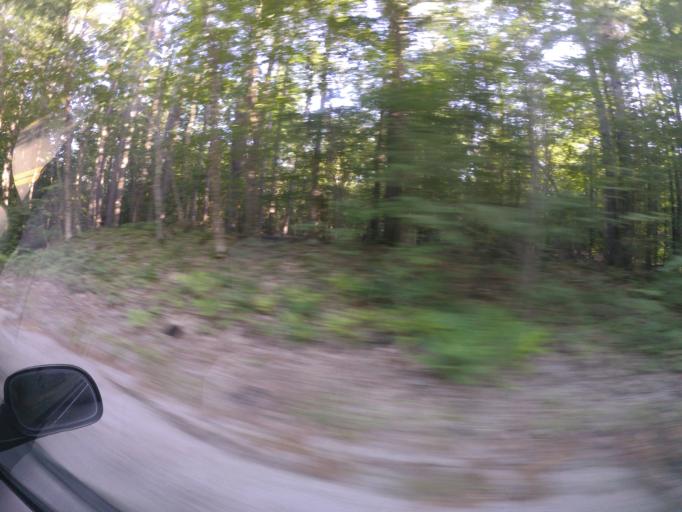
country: US
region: Maine
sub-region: Cumberland County
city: Raymond
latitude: 43.8896
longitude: -70.4350
